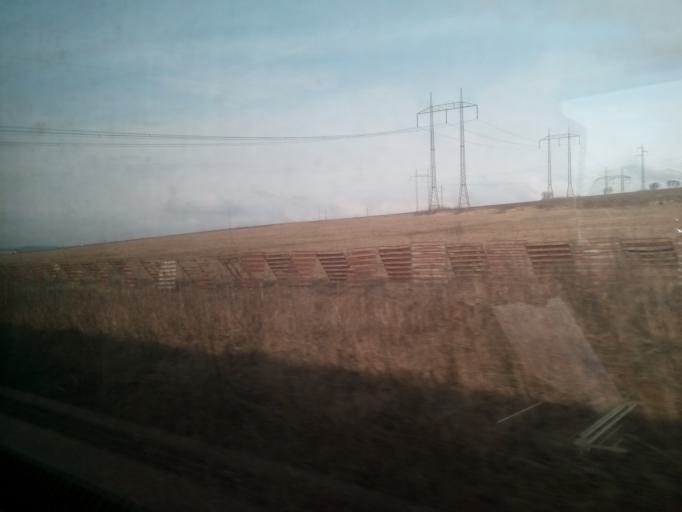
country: SK
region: Presovsky
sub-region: Okres Poprad
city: Strba
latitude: 49.0724
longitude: 20.0104
